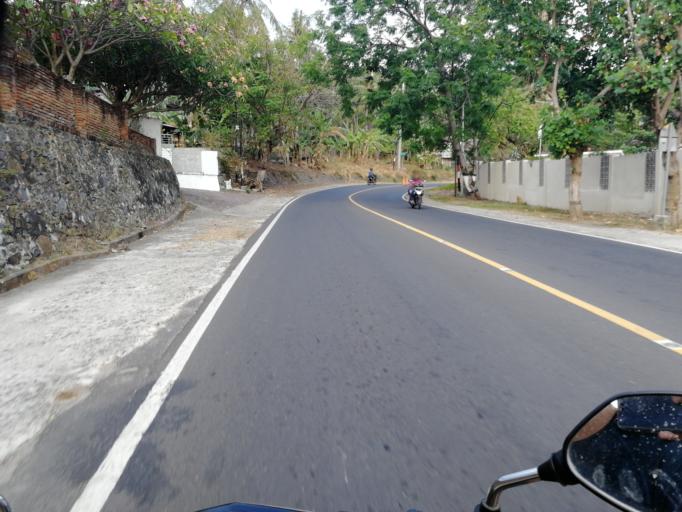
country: ID
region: West Nusa Tenggara
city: Mambalan
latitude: -8.4946
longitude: 116.0392
